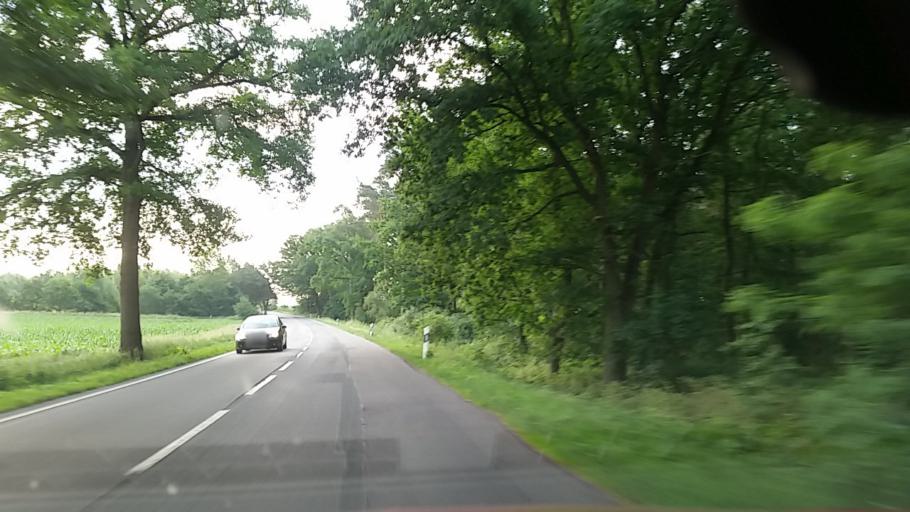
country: DE
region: Lower Saxony
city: Rennau
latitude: 52.2996
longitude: 10.8792
